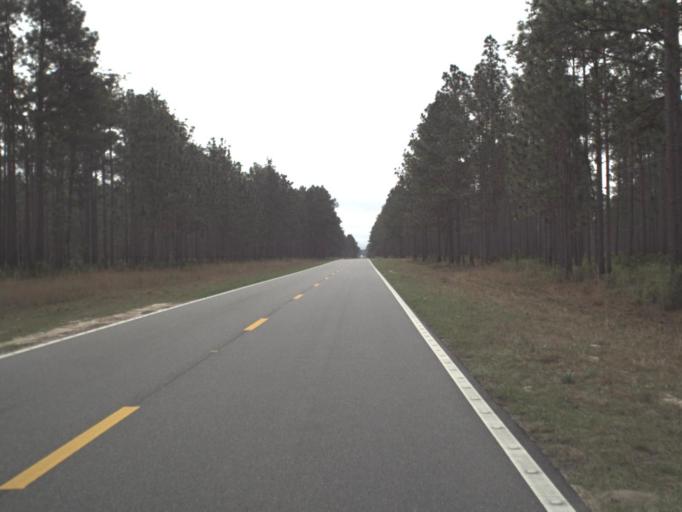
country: US
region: Florida
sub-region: Gulf County
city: Wewahitchka
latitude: 30.1184
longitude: -84.9881
